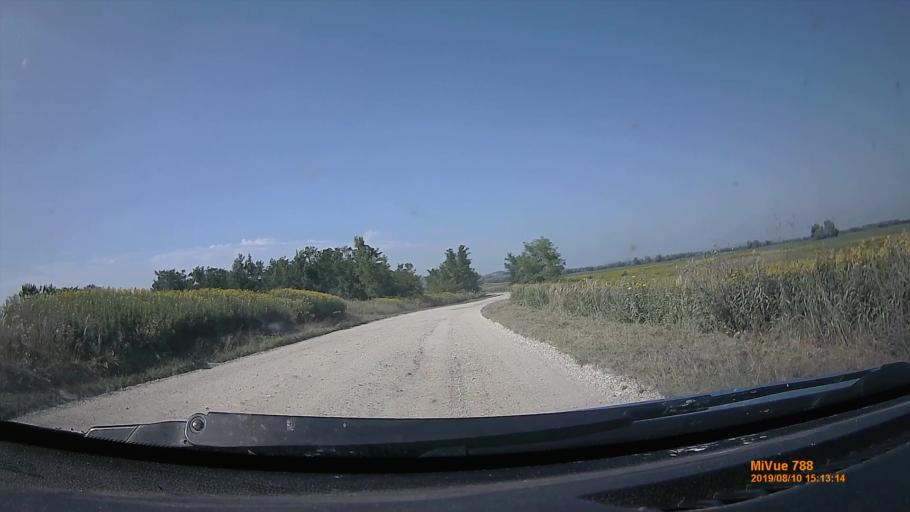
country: HU
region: Somogy
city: Fonyod
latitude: 46.6912
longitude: 17.5616
